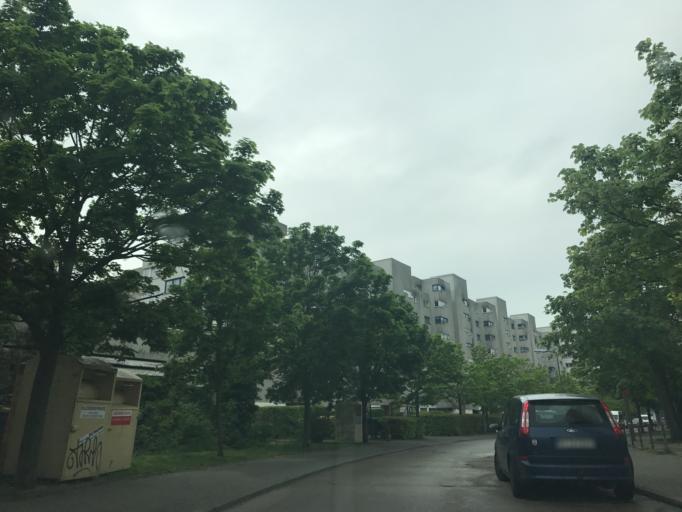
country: DE
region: Berlin
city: Wilhelmstadt
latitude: 52.5216
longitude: 13.1617
